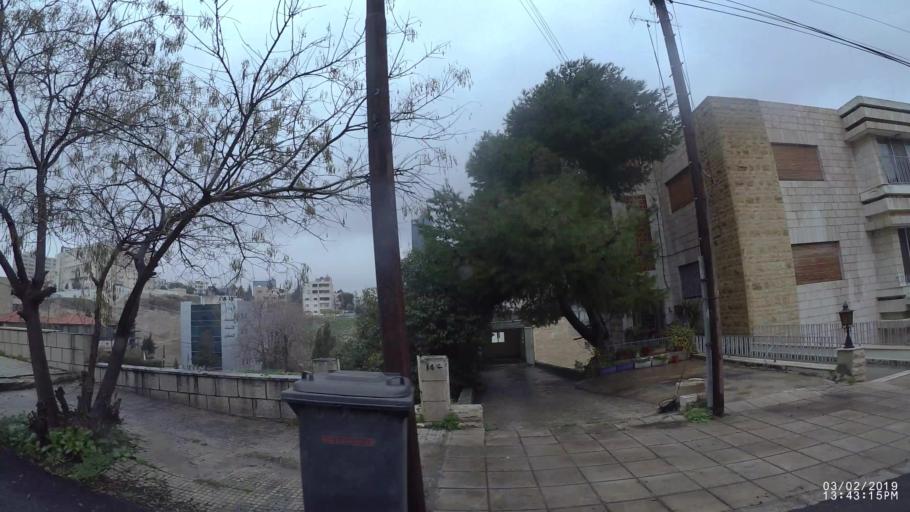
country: JO
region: Amman
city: Amman
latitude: 31.9583
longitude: 35.9026
